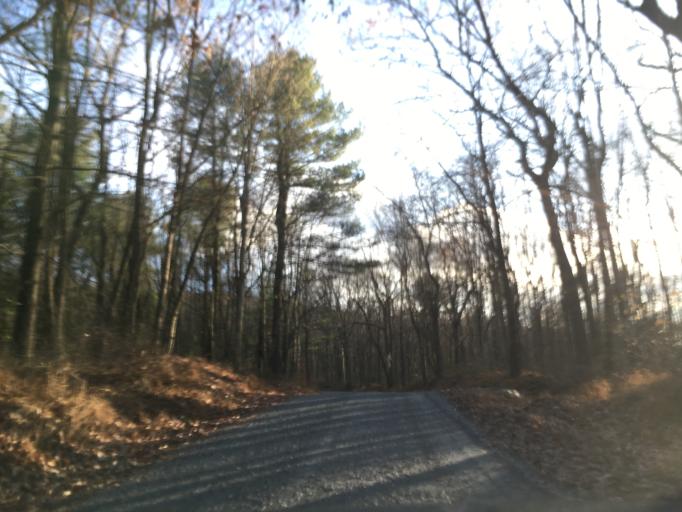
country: US
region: Pennsylvania
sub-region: Carbon County
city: Lehighton
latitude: 40.7714
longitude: -75.7105
